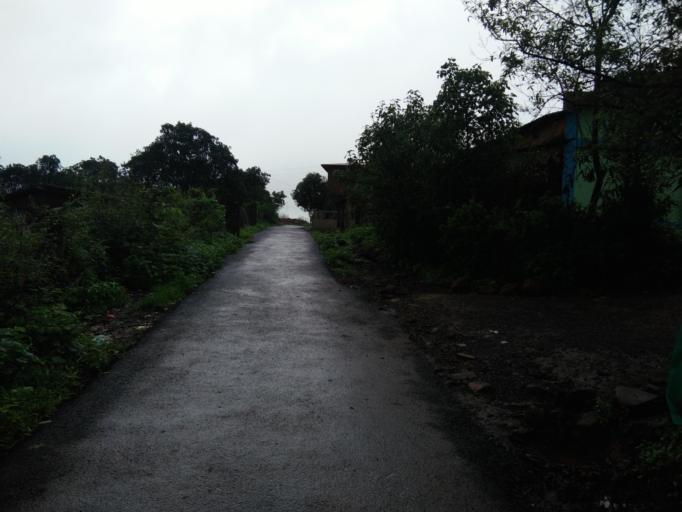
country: IN
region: Maharashtra
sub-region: Thane
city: Jawhar
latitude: 19.9219
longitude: 73.2259
